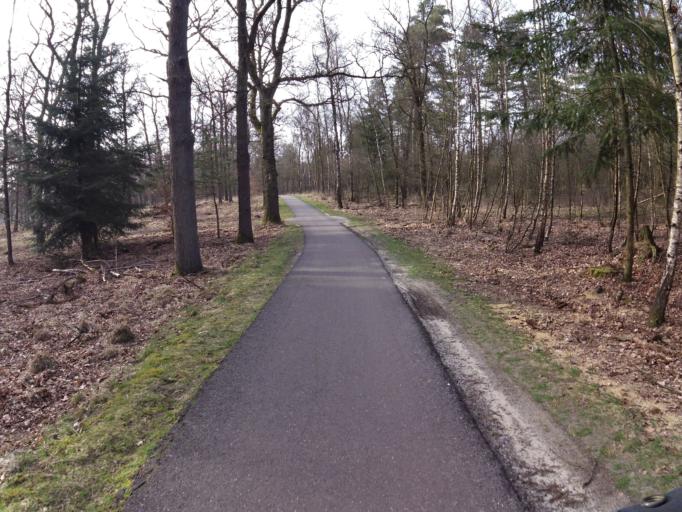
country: NL
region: Gelderland
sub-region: Gemeente Ede
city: Otterlo
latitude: 52.1065
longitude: 5.8509
